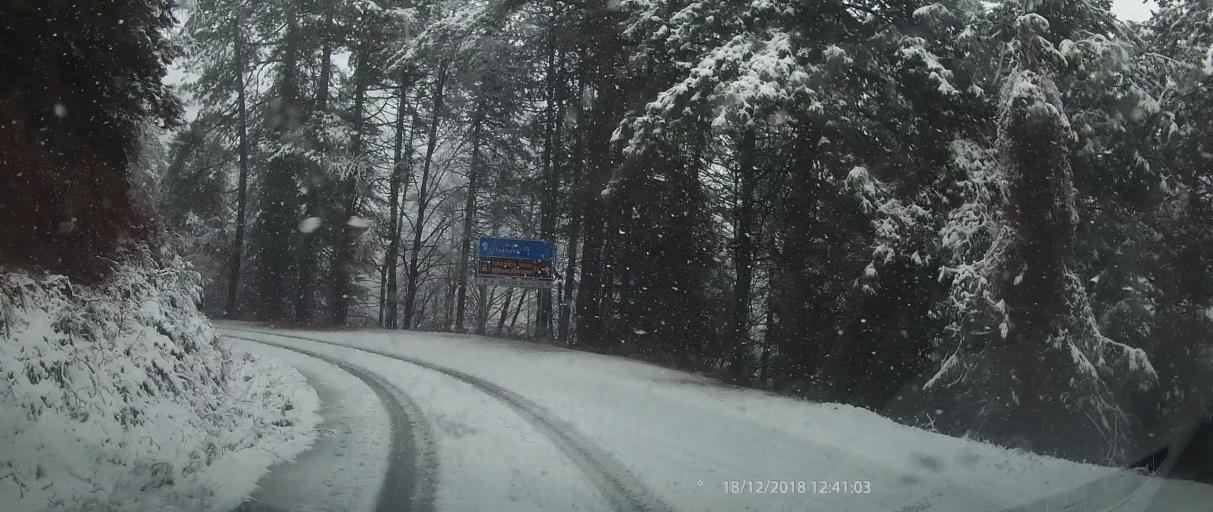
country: GR
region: Central Macedonia
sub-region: Nomos Pierias
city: Litochoro
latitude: 40.0925
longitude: 22.4196
